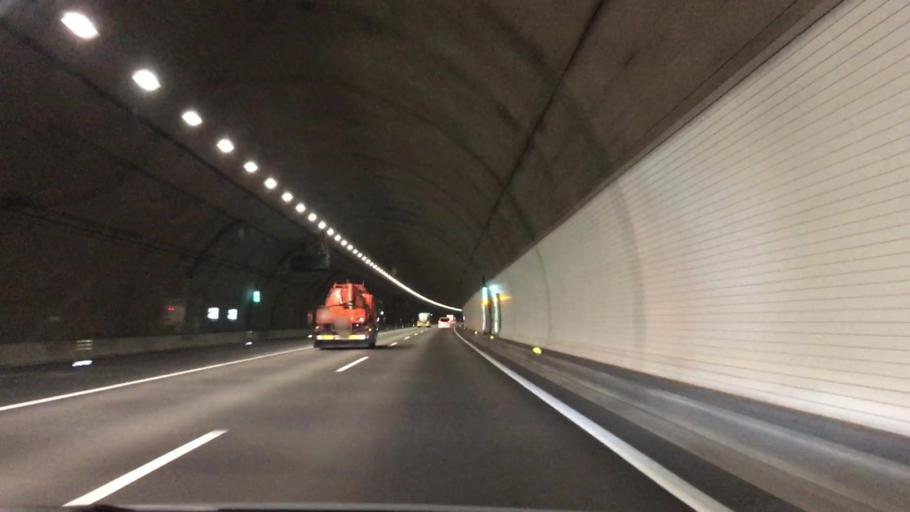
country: JP
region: Shizuoka
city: Hamakita
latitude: 34.8759
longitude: 137.6685
